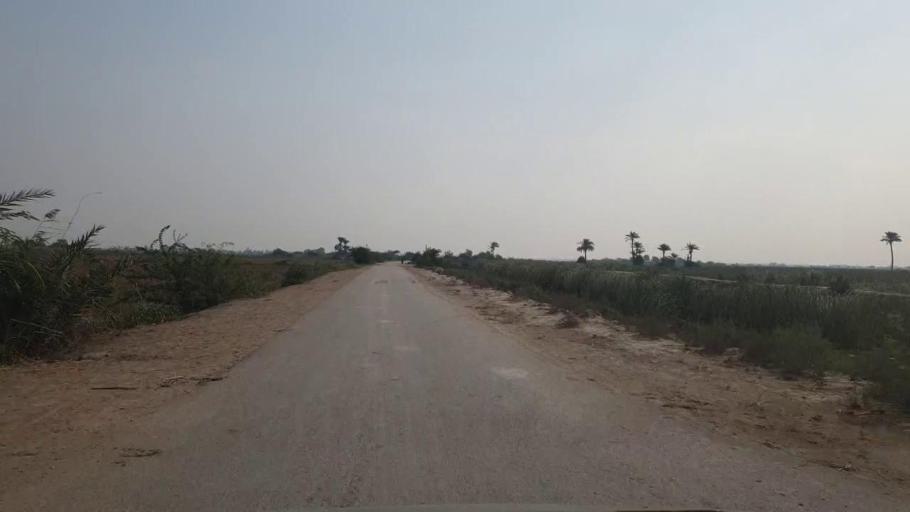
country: PK
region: Sindh
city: Tando Muhammad Khan
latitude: 25.0973
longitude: 68.3787
